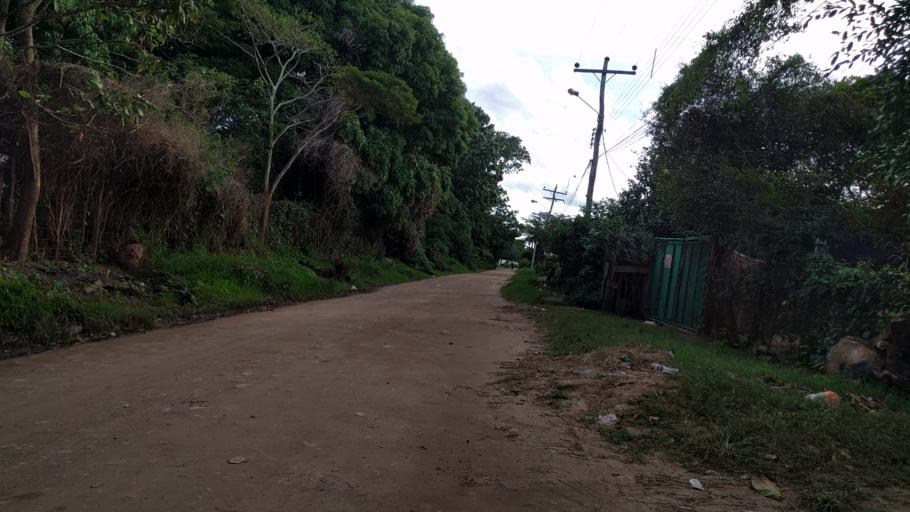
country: BO
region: Santa Cruz
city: Santa Cruz de la Sierra
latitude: -17.8498
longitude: -63.2537
